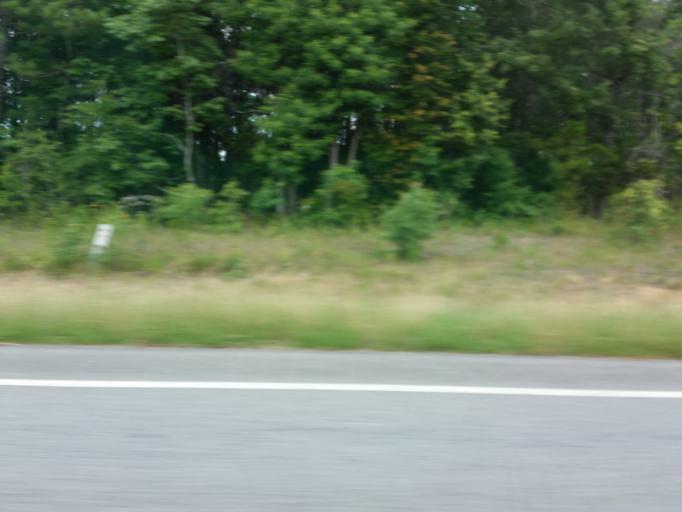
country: US
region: Alabama
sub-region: Sumter County
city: York
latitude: 32.4026
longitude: -88.2182
